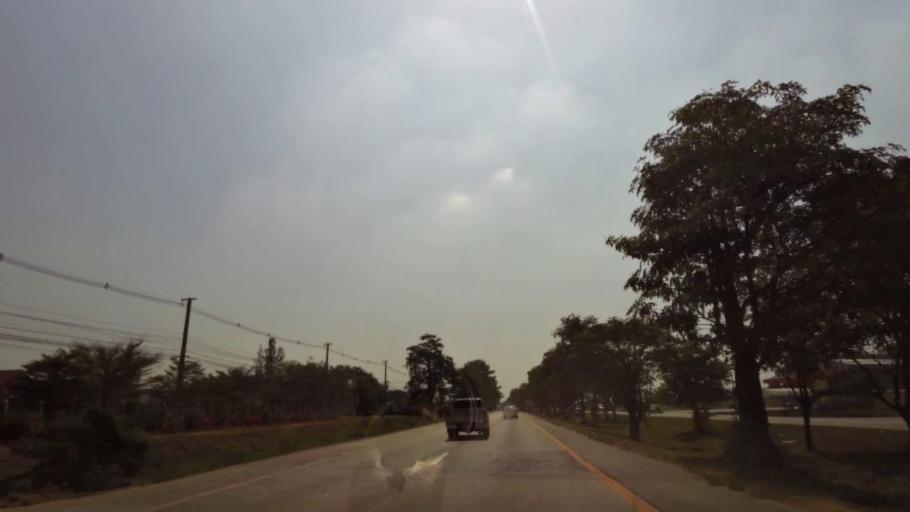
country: TH
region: Phichit
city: Wachira Barami
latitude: 16.5187
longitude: 100.1429
